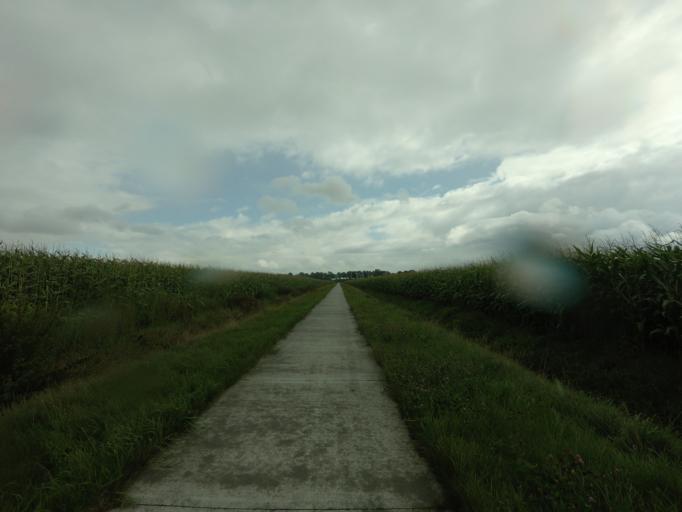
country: NL
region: Drenthe
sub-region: Gemeente Westerveld
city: Dwingeloo
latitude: 52.9761
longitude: 6.3563
